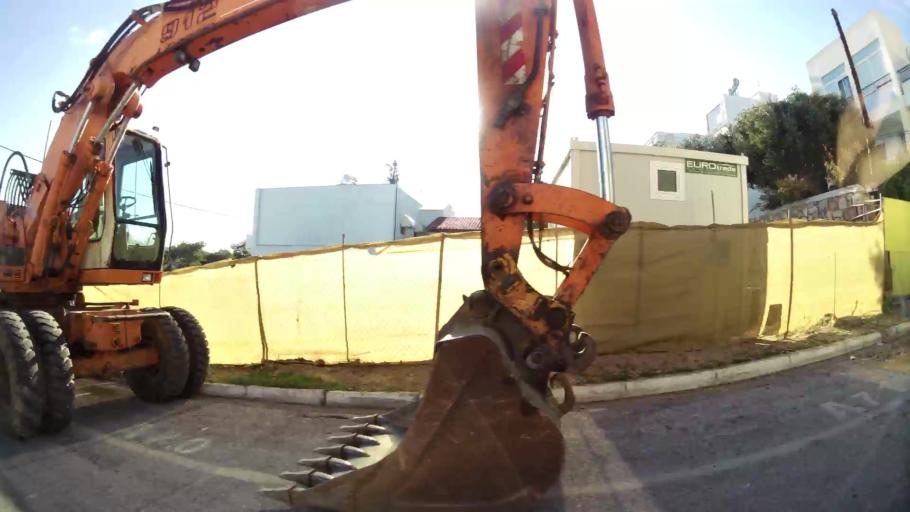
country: GR
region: Attica
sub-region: Nomarchia Anatolikis Attikis
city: Rafina
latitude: 38.0232
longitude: 24.0086
